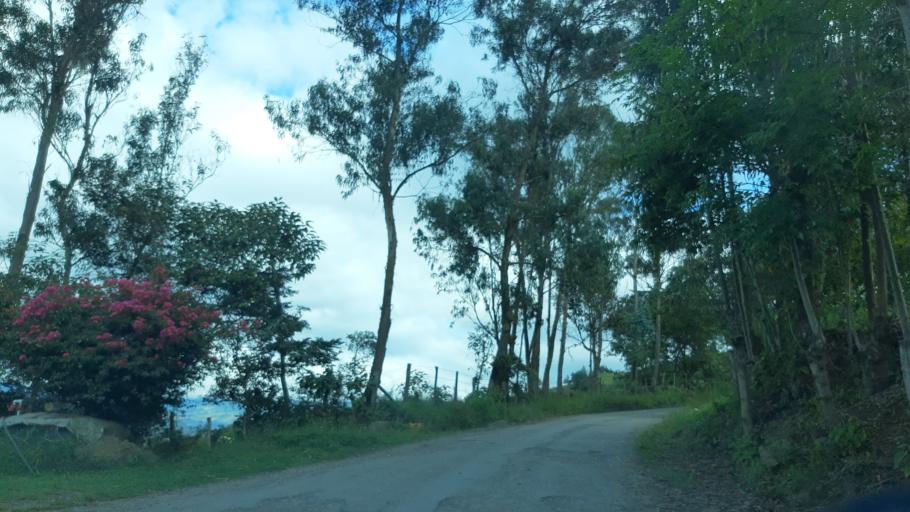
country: CO
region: Cundinamarca
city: Tenza
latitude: 5.0449
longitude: -73.4175
